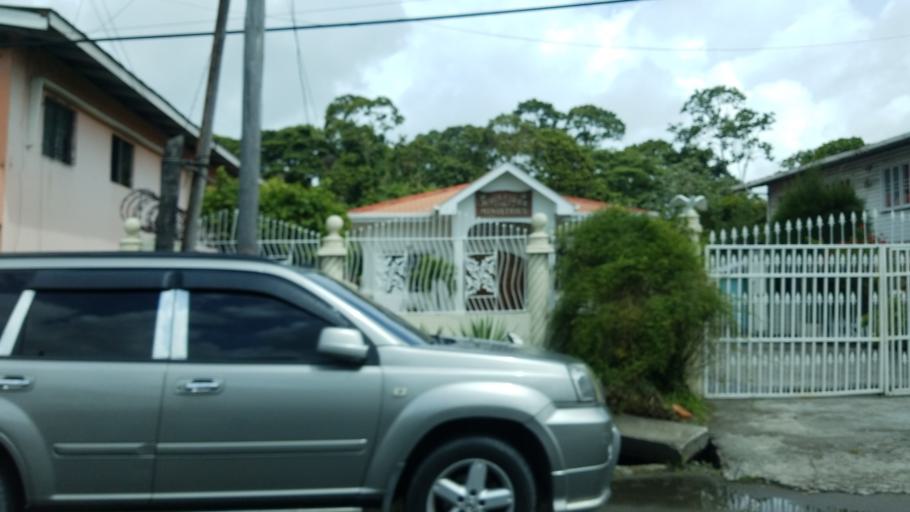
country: GY
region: Demerara-Mahaica
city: Georgetown
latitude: 6.7798
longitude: -58.1707
